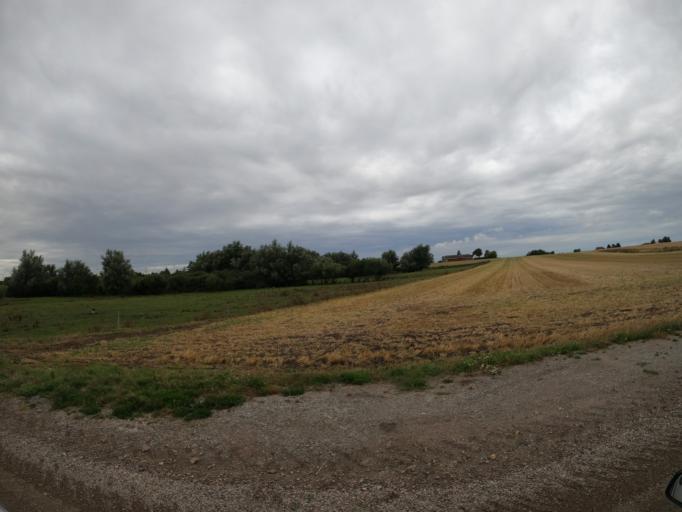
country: SE
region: Skane
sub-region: Kavlinge Kommun
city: Kaevlinge
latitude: 55.7576
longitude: 13.1267
